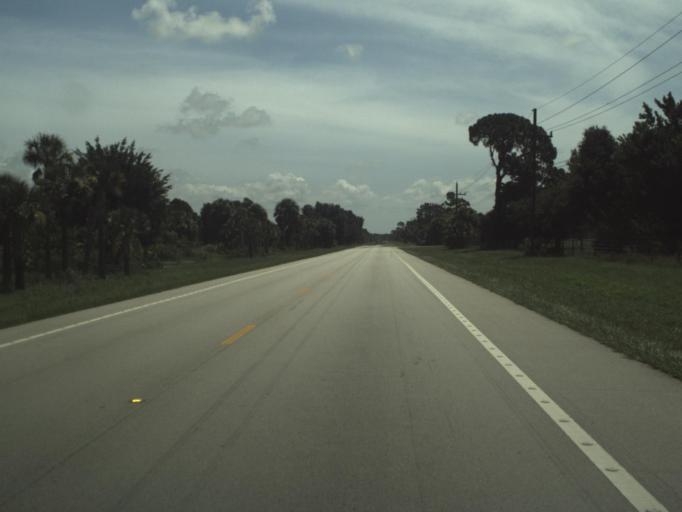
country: US
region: Florida
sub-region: Martin County
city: Indiantown
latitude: 27.0054
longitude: -80.5625
